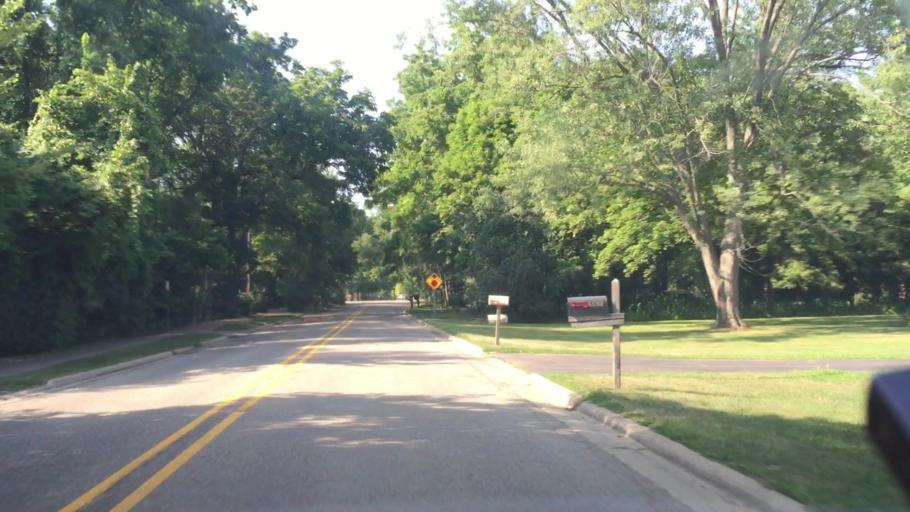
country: US
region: Michigan
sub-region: Oakland County
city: Franklin
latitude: 42.5430
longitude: -83.2969
